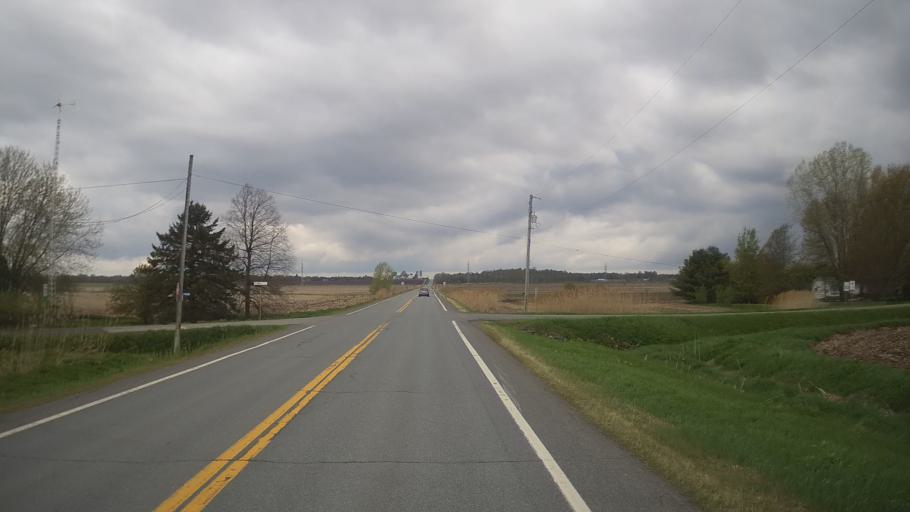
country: CA
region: Quebec
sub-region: Monteregie
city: Farnham
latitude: 45.2580
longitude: -72.9192
